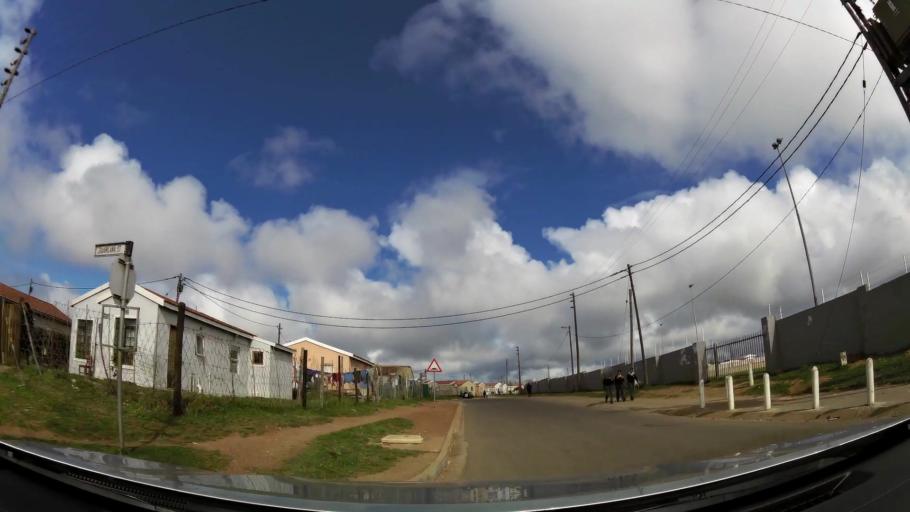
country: ZA
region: Western Cape
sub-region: Eden District Municipality
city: Plettenberg Bay
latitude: -34.0539
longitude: 23.3185
